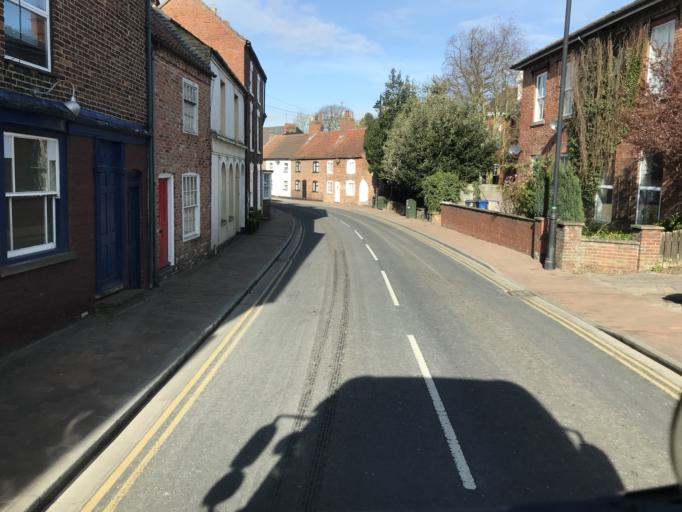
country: GB
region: England
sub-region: Lincolnshire
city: Market Rasen
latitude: 53.3882
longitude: -0.3391
